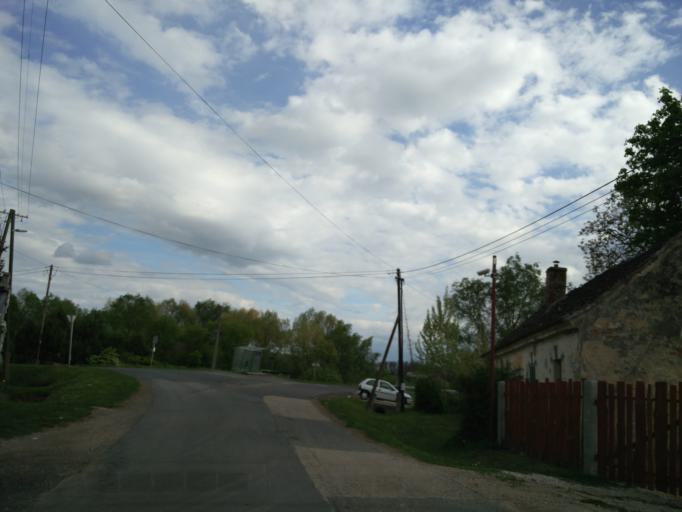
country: HU
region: Zala
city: Zalaegerszeg
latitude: 46.8825
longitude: 16.9221
